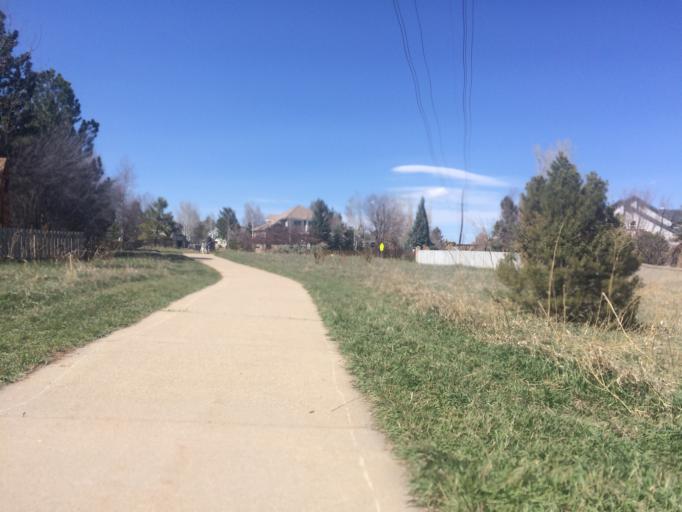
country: US
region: Colorado
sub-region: Boulder County
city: Louisville
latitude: 39.9778
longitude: -105.1562
